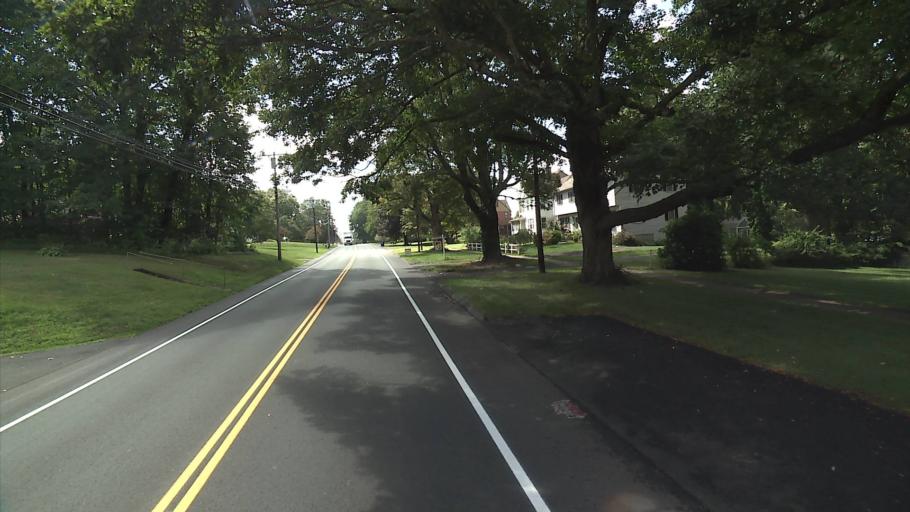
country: US
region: Connecticut
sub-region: Middlesex County
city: Portland
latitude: 41.5848
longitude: -72.6314
